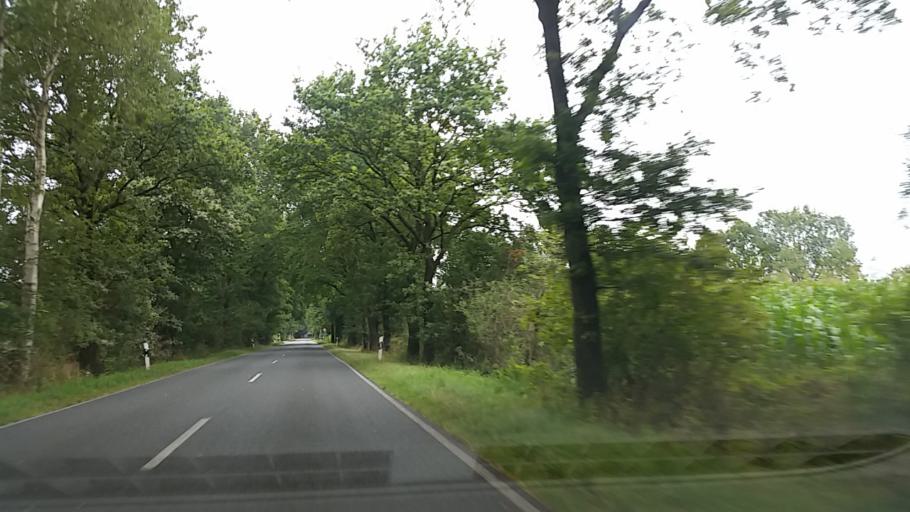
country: DE
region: Lower Saxony
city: Vollersode
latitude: 53.4095
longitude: 8.9169
